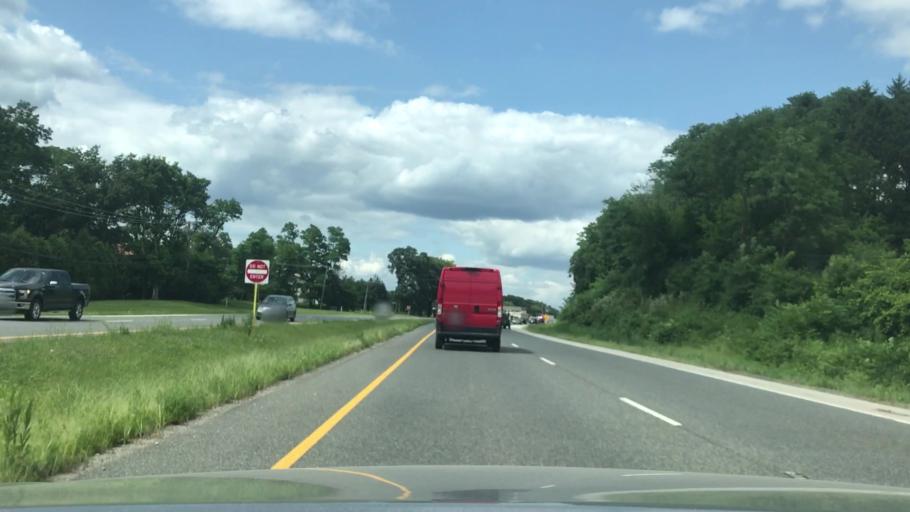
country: US
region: Illinois
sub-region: DuPage County
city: Burr Ridge
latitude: 41.7141
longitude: -87.9449
